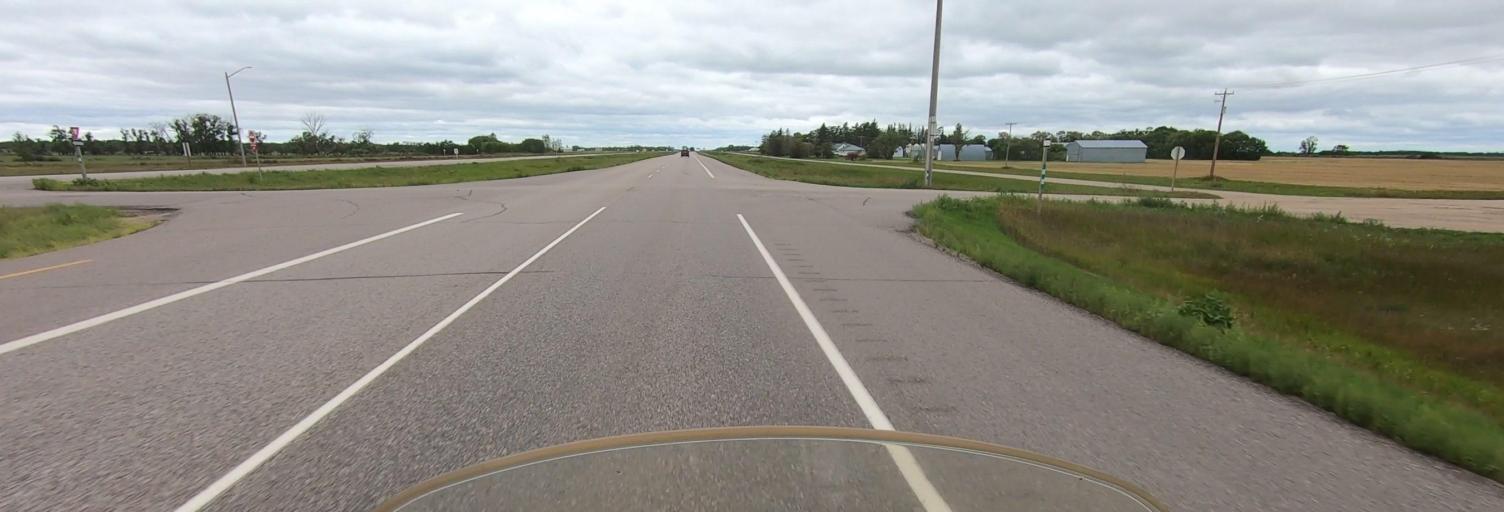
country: CA
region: Manitoba
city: Portage la Prairie
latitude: 49.9752
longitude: -98.6286
